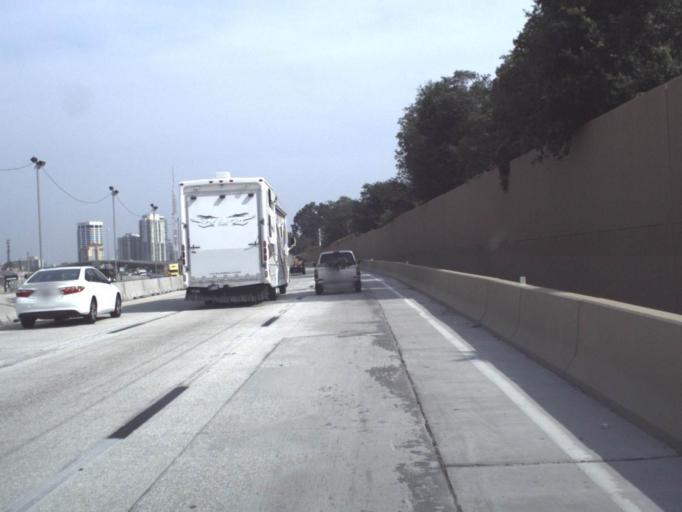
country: US
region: Florida
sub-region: Duval County
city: Jacksonville
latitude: 30.3031
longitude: -81.6413
